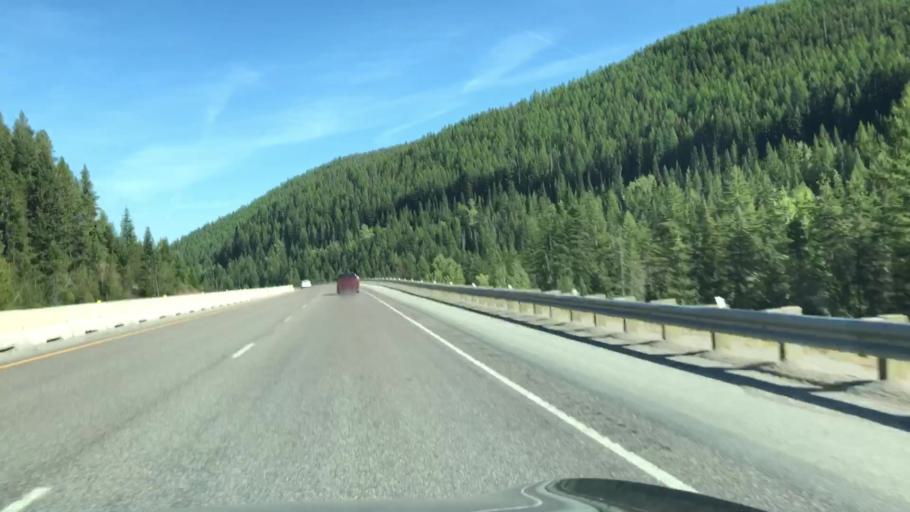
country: US
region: Montana
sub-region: Sanders County
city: Thompson Falls
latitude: 47.4161
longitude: -115.5786
